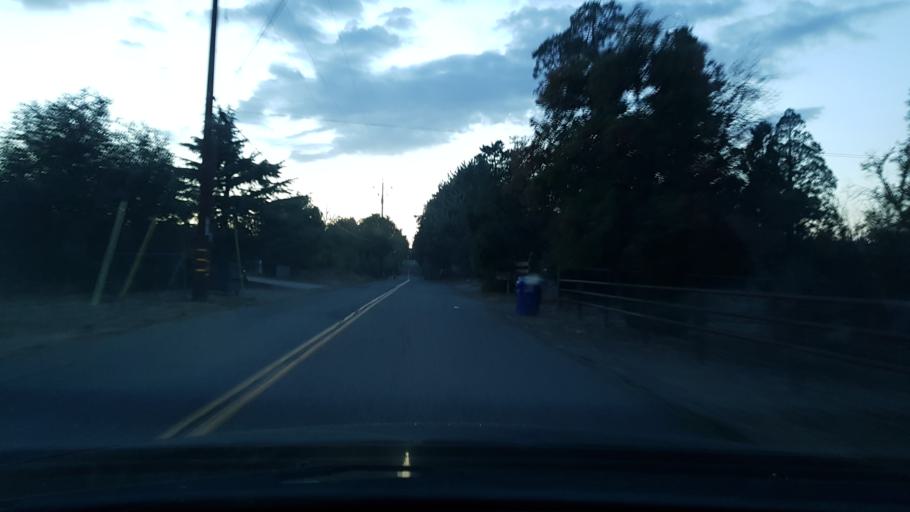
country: US
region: California
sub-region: San Diego County
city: Julian
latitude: 33.0943
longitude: -116.6418
